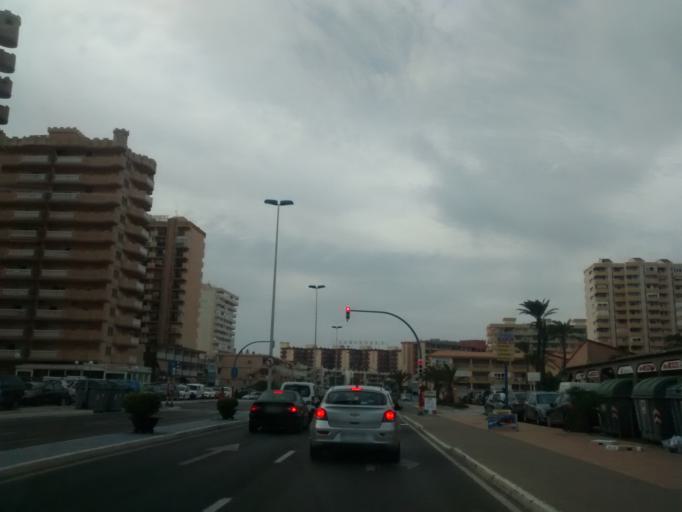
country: ES
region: Murcia
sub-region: Murcia
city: La Manga del Mar Menor
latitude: 37.6783
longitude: -0.7332
